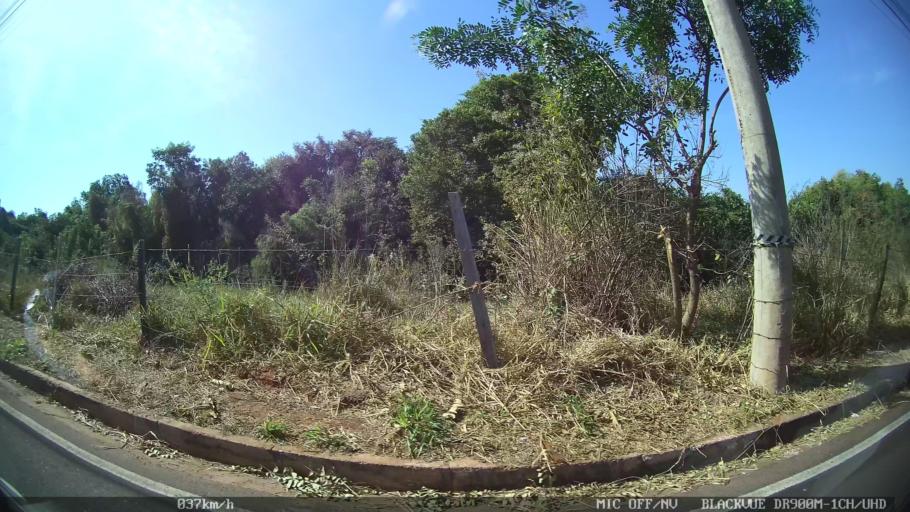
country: BR
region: Sao Paulo
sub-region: Sao Jose Do Rio Preto
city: Sao Jose do Rio Preto
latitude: -20.7880
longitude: -49.4291
